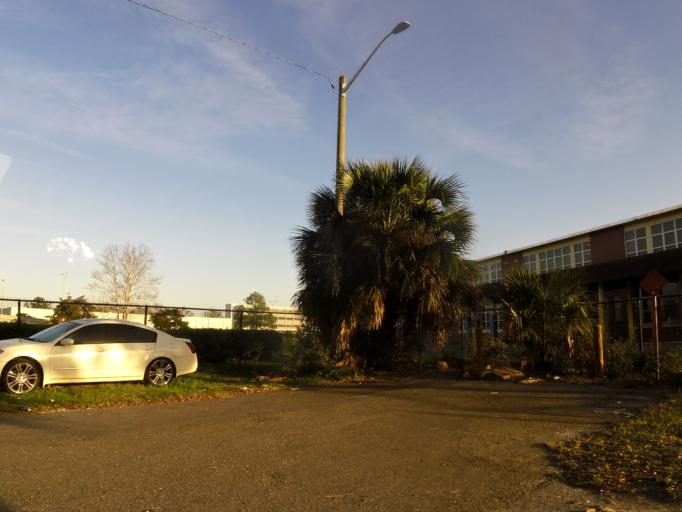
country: US
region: Florida
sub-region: Duval County
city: Jacksonville
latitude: 30.3429
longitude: -81.6383
